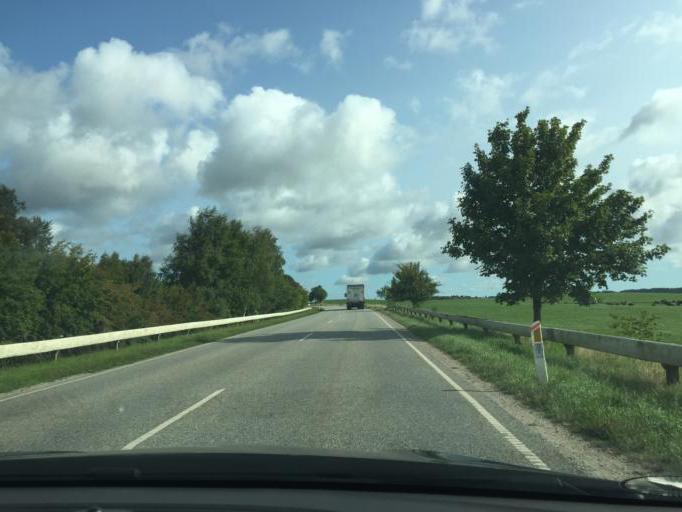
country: DK
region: Central Jutland
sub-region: Odder Kommune
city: Odder
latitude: 55.8991
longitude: 10.0186
